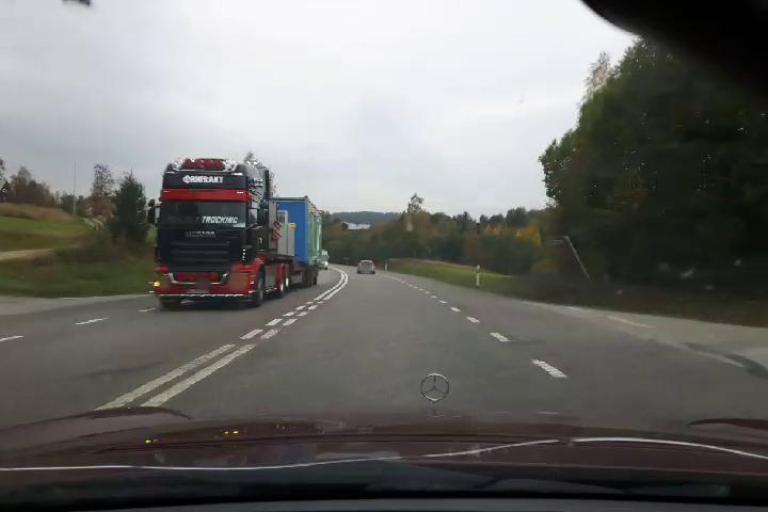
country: SE
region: Vaesternorrland
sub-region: Kramfors Kommun
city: Nordingra
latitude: 63.0226
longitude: 18.2969
